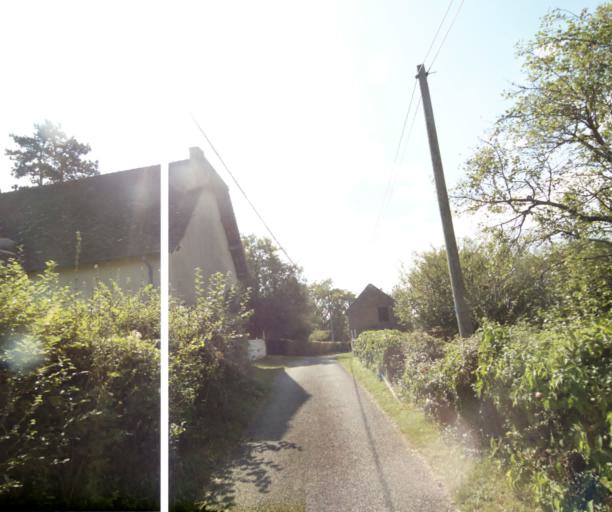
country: FR
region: Bourgogne
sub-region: Departement de Saone-et-Loire
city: Charolles
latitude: 46.3912
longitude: 4.2573
